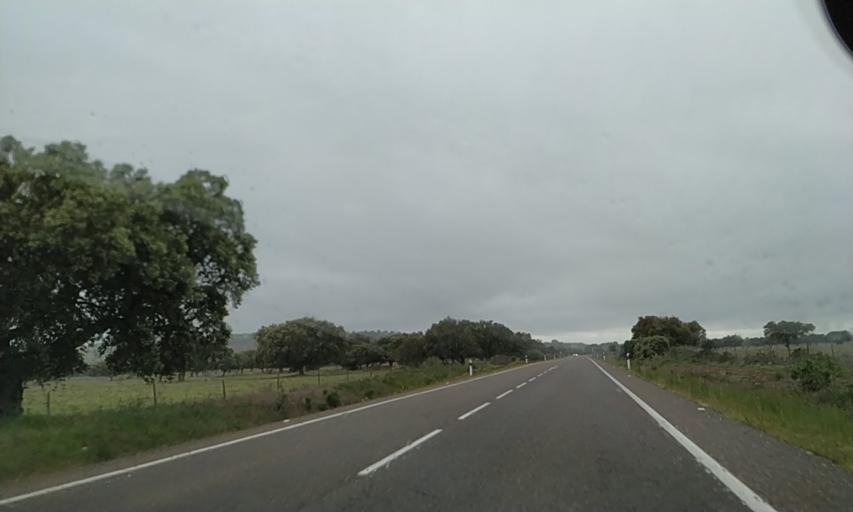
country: ES
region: Extremadura
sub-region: Provincia de Badajoz
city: La Roca de la Sierra
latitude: 39.0942
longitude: -6.7158
